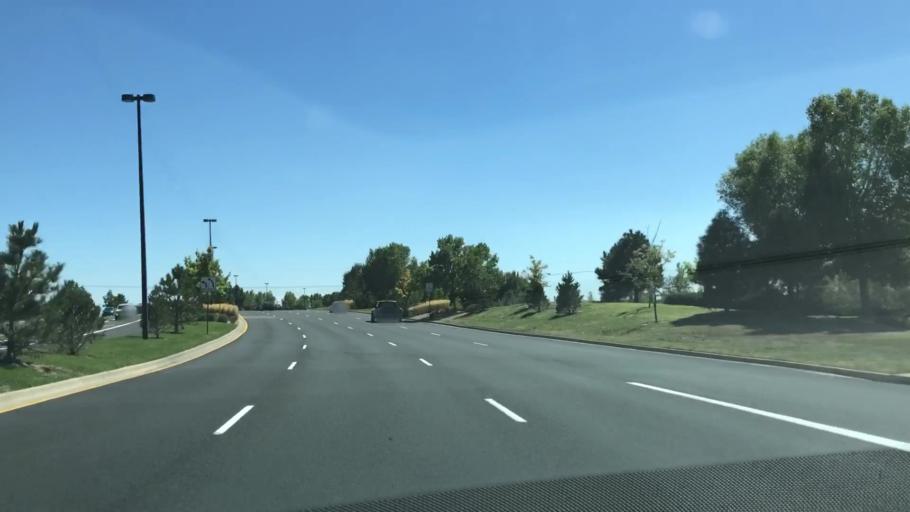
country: US
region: Colorado
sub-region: Larimer County
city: Loveland
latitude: 40.4110
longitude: -104.9859
